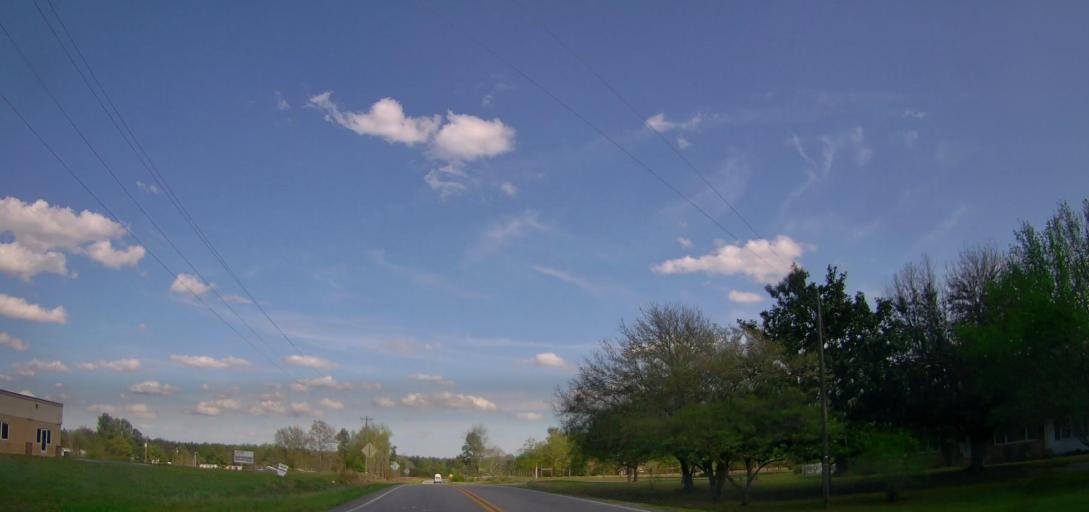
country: US
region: Georgia
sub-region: Baldwin County
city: Hardwick
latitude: 33.0795
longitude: -83.1459
